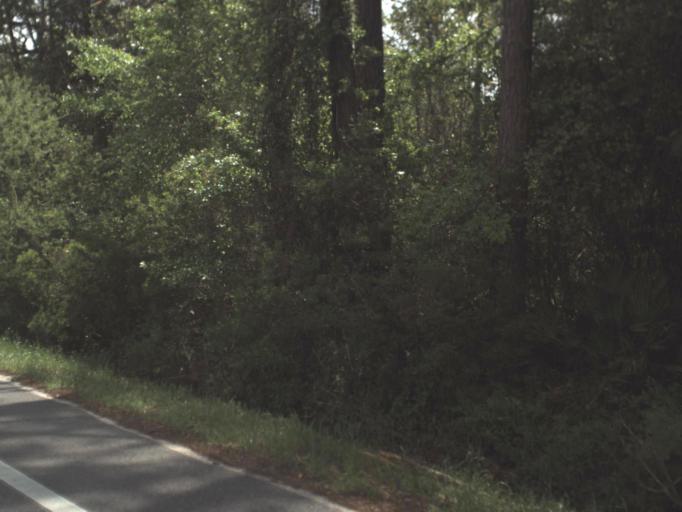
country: US
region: Florida
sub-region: Escambia County
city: Myrtle Grove
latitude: 30.3703
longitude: -87.3321
